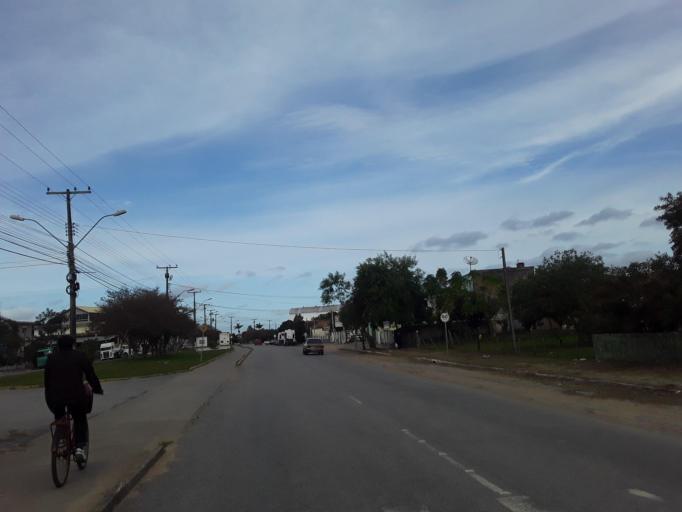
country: BR
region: Rio Grande do Sul
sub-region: Sao Lourenco Do Sul
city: Sao Lourenco do Sul
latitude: -31.3511
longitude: -51.9906
